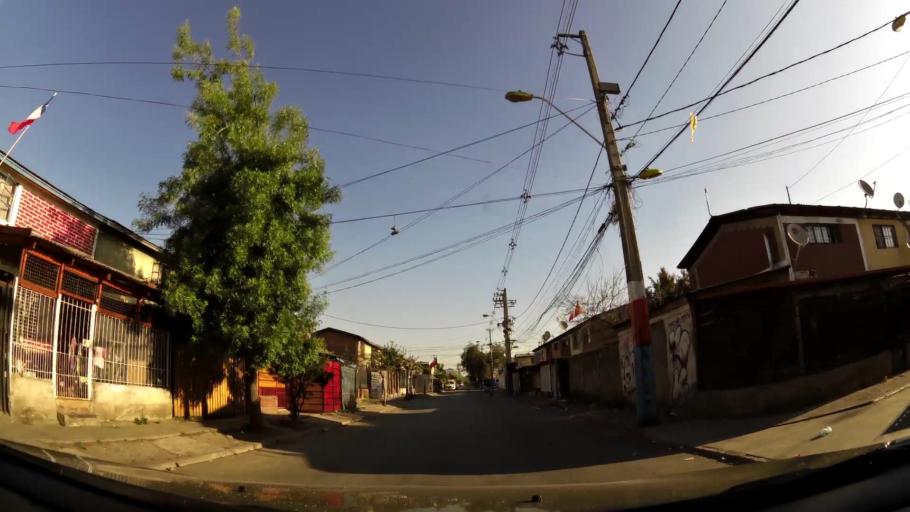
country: CL
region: Santiago Metropolitan
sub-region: Provincia de Santiago
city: La Pintana
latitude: -33.5803
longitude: -70.6660
